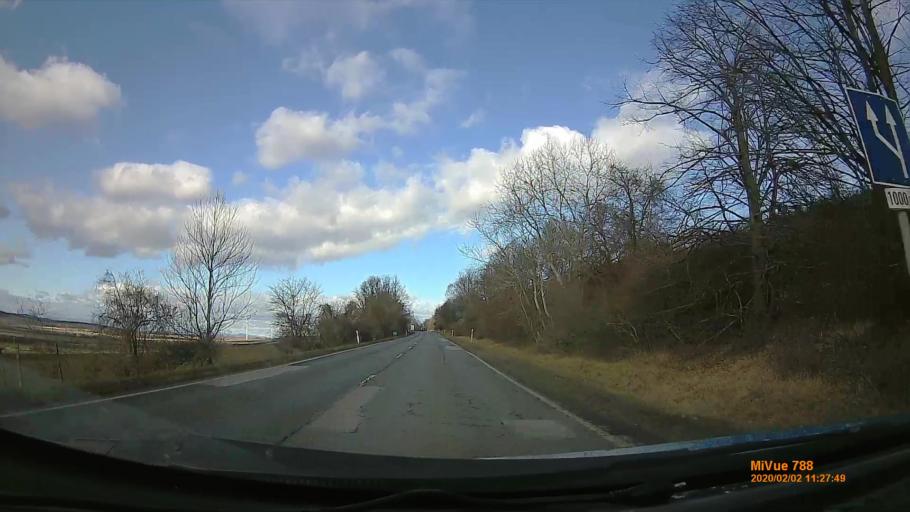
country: AT
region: Burgenland
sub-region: Eisenstadt-Umgebung
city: Klingenbach
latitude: 47.7215
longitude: 16.5649
